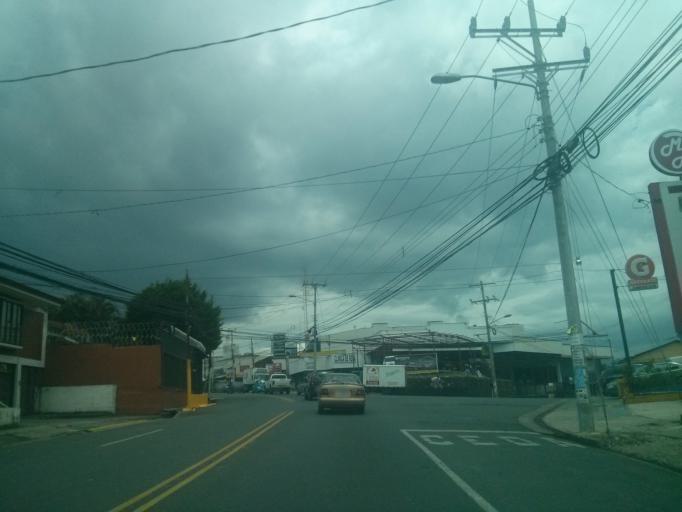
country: CR
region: San Jose
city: San Pedro
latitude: 9.9252
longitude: -84.0614
